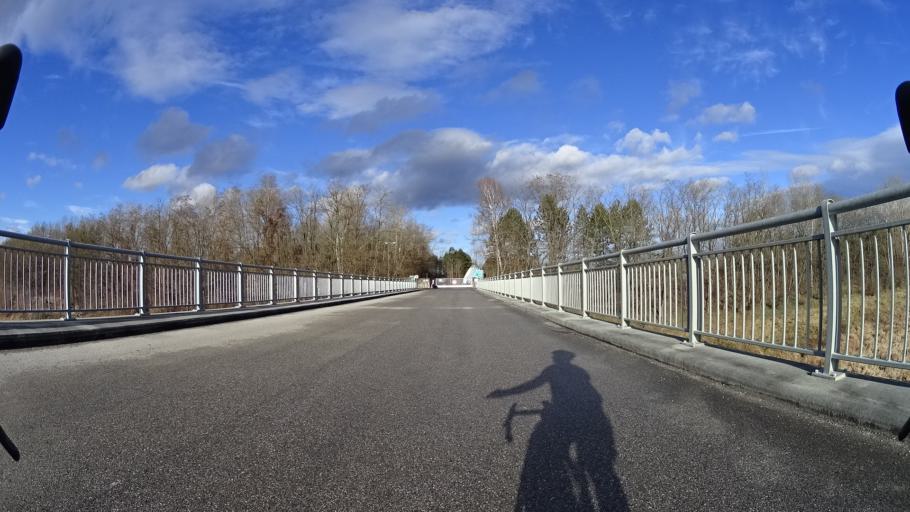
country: AT
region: Lower Austria
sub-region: Politischer Bezirk Tulln
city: Kirchberg am Wagram
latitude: 48.3698
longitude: 15.8549
